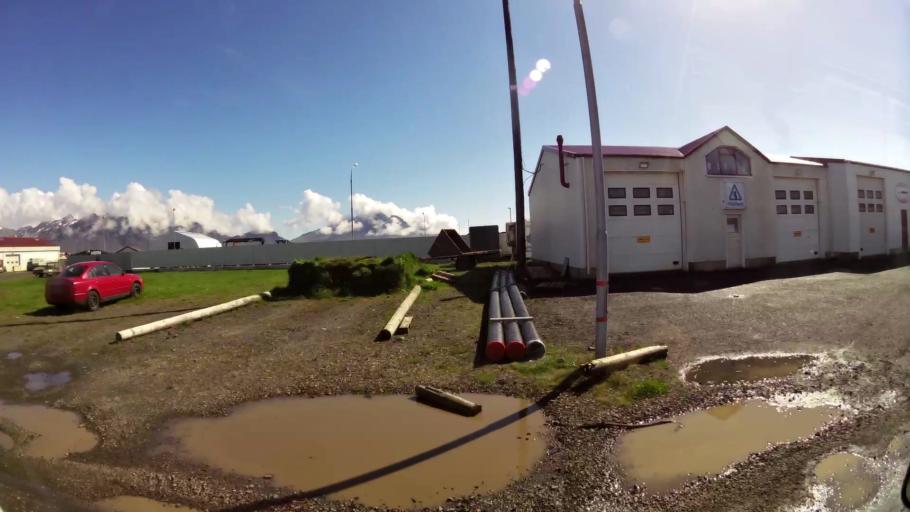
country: IS
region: East
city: Hoefn
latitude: 64.2523
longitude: -15.1996
